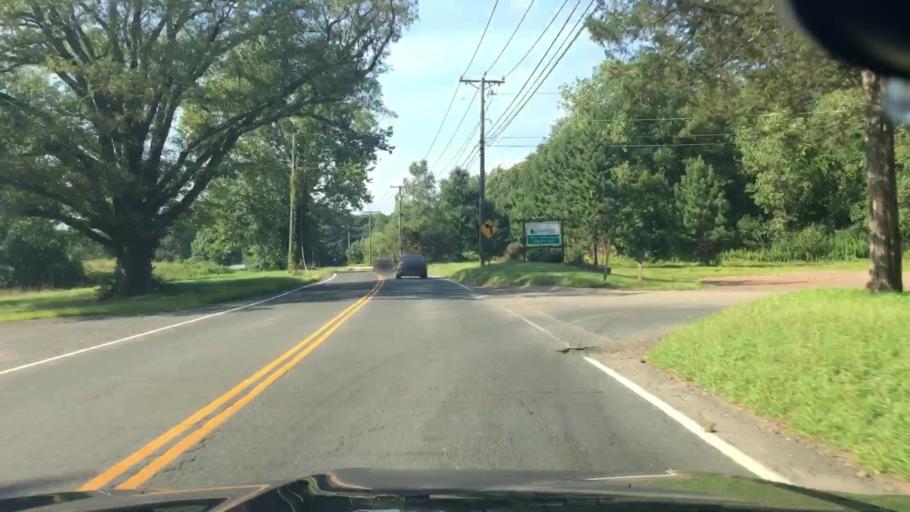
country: US
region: Connecticut
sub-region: Hartford County
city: Broad Brook
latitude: 41.9346
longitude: -72.5116
